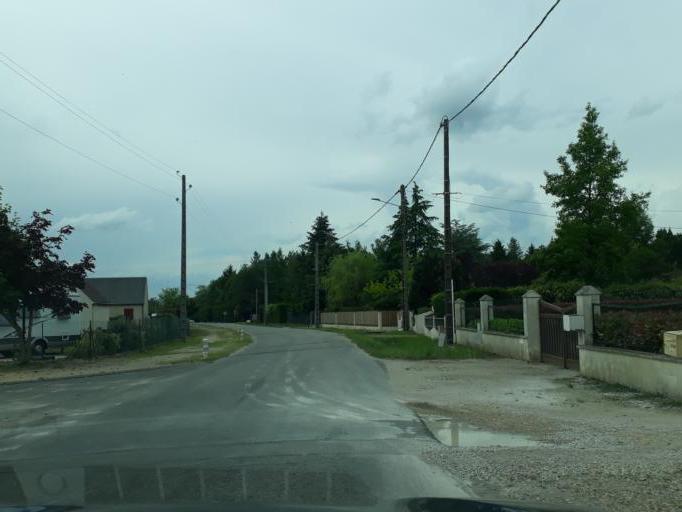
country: FR
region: Centre
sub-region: Departement du Loiret
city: Tigy
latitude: 47.7899
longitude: 2.2079
